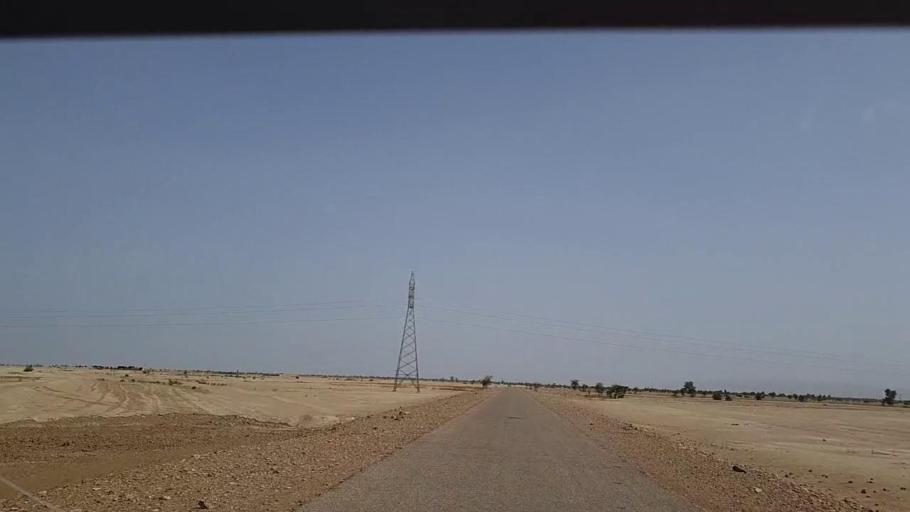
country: PK
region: Sindh
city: Johi
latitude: 26.6697
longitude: 67.5084
